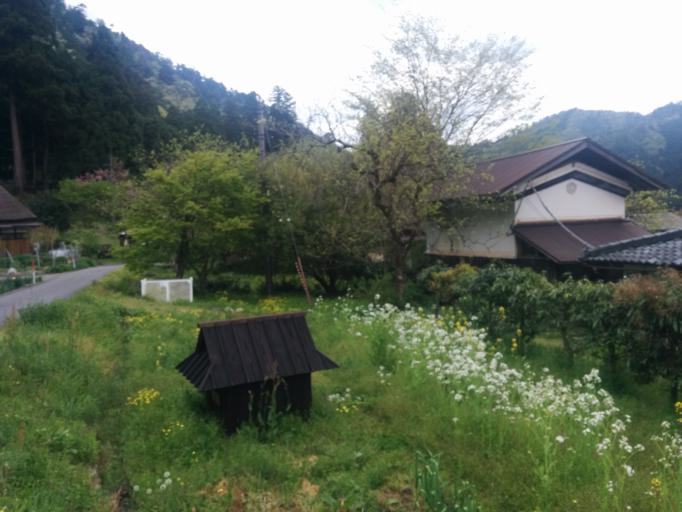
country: JP
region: Fukui
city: Obama
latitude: 35.3141
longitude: 135.6235
